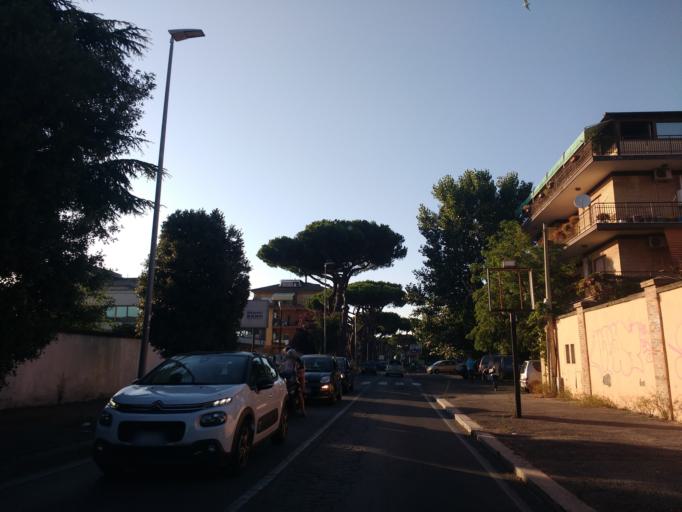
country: IT
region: Latium
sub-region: Citta metropolitana di Roma Capitale
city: Acilia-Castel Fusano-Ostia Antica
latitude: 41.7769
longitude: 12.3692
